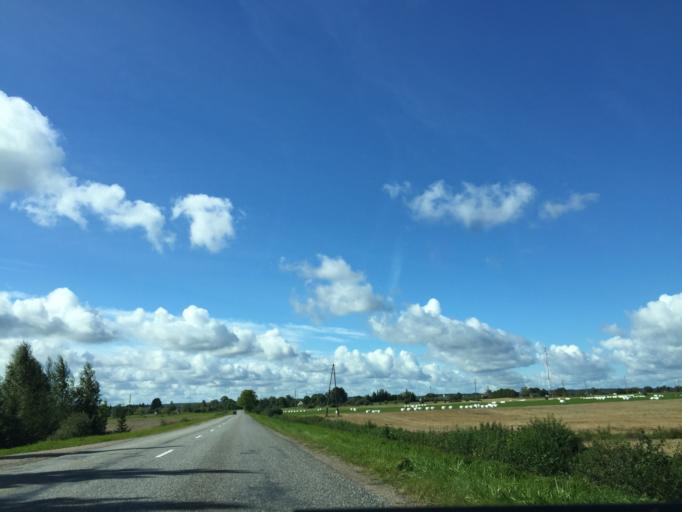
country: LV
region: Kuldigas Rajons
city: Kuldiga
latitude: 56.9767
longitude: 22.0080
